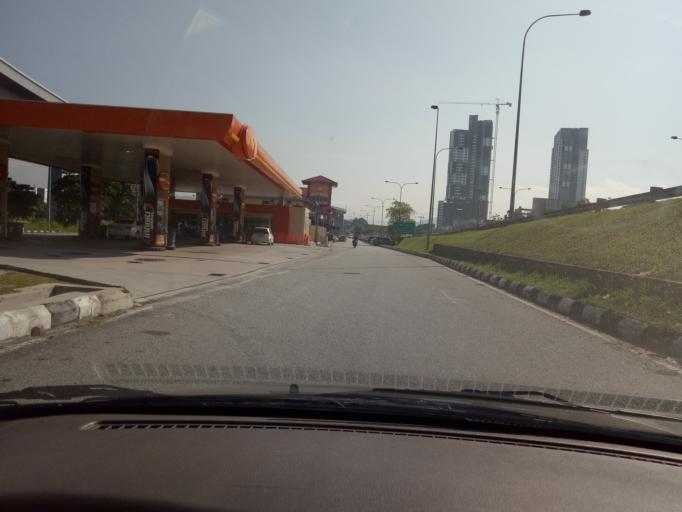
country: MY
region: Selangor
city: Kampong Baharu Balakong
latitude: 3.0317
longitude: 101.7691
